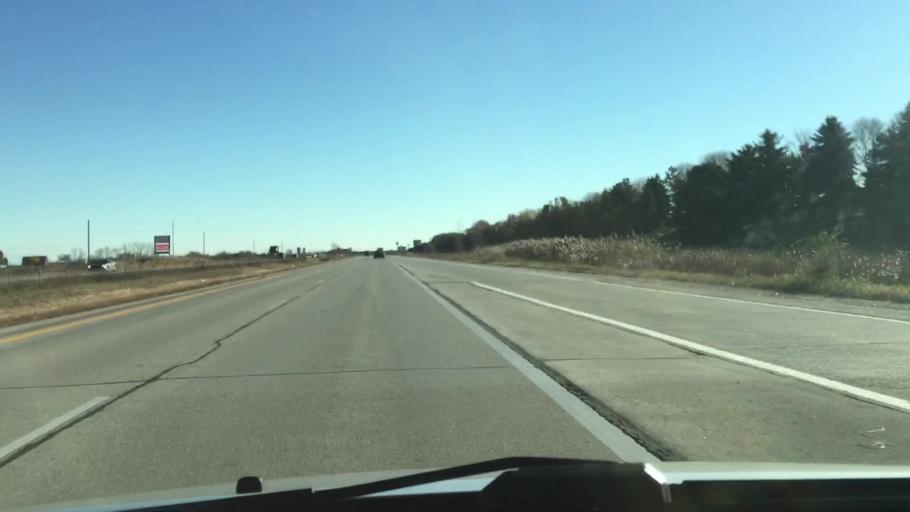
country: US
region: Wisconsin
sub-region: Outagamie County
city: Kimberly
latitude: 44.2979
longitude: -88.3516
